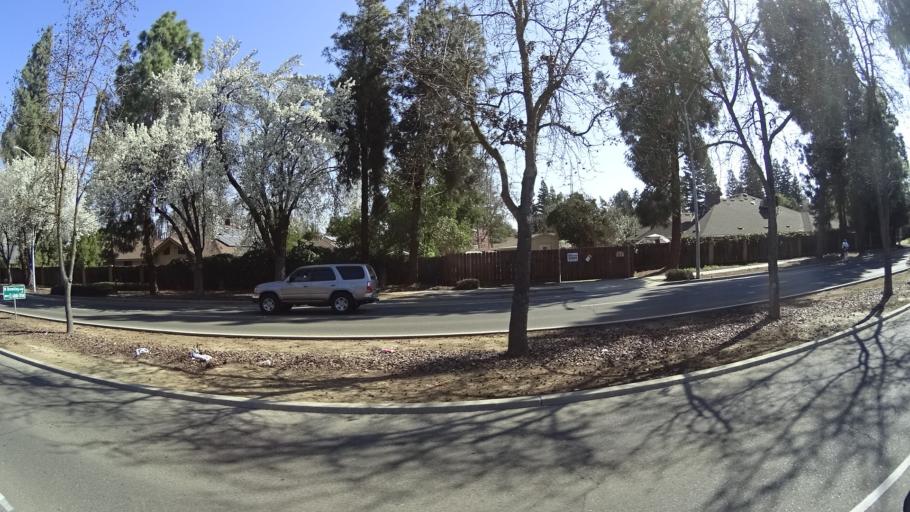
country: US
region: California
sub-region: Fresno County
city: Fresno
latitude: 36.8179
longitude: -119.8265
